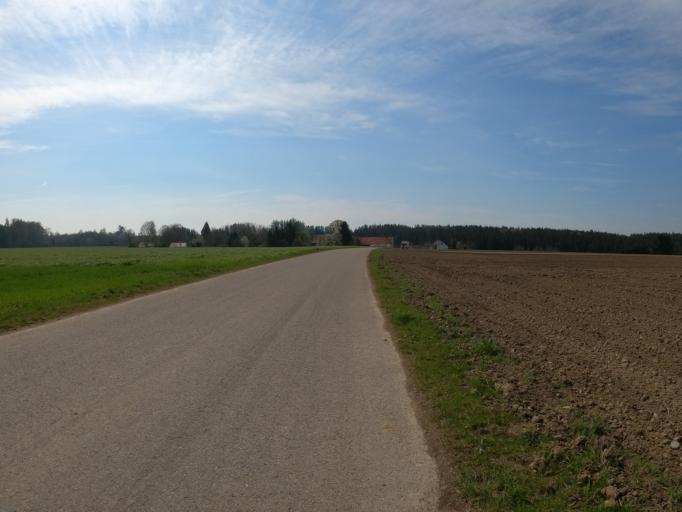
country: DE
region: Bavaria
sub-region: Swabia
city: Rieden an der Kotz
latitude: 48.3726
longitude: 10.2179
